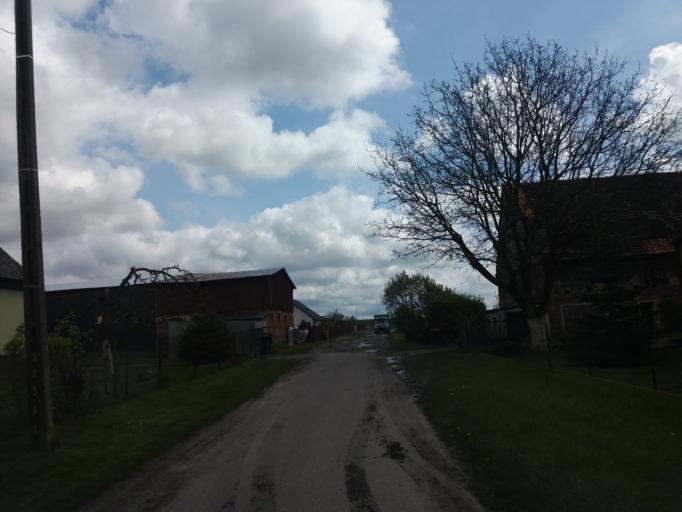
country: PL
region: West Pomeranian Voivodeship
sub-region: Powiat choszczenski
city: Choszczno
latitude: 53.2094
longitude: 15.3981
